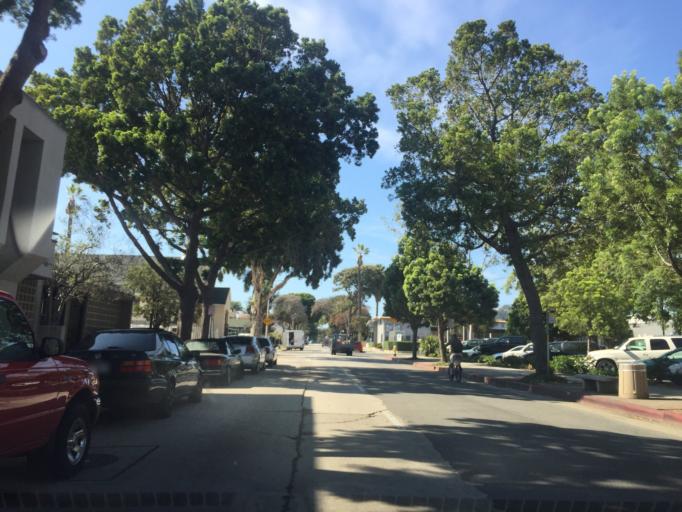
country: US
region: California
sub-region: Santa Barbara County
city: Santa Barbara
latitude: 34.4186
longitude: -119.6914
